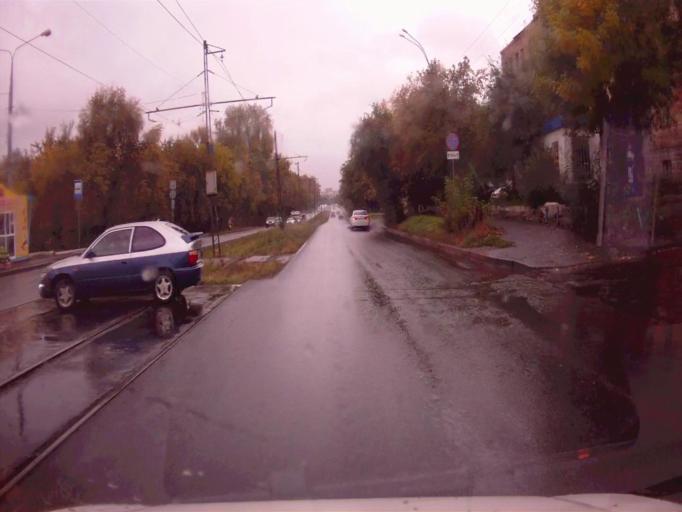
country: RU
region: Chelyabinsk
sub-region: Gorod Chelyabinsk
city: Chelyabinsk
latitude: 55.1779
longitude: 61.4149
